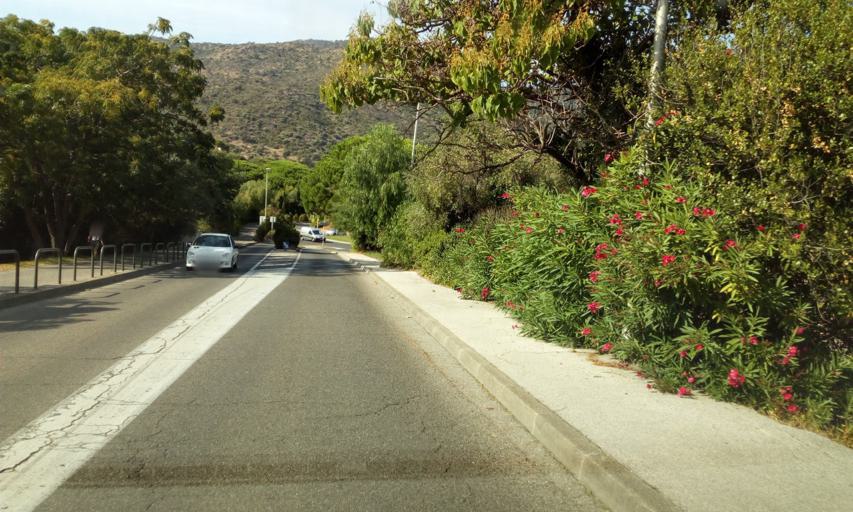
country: FR
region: Provence-Alpes-Cote d'Azur
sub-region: Departement du Var
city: Le Lavandou
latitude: 43.1401
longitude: 6.3799
